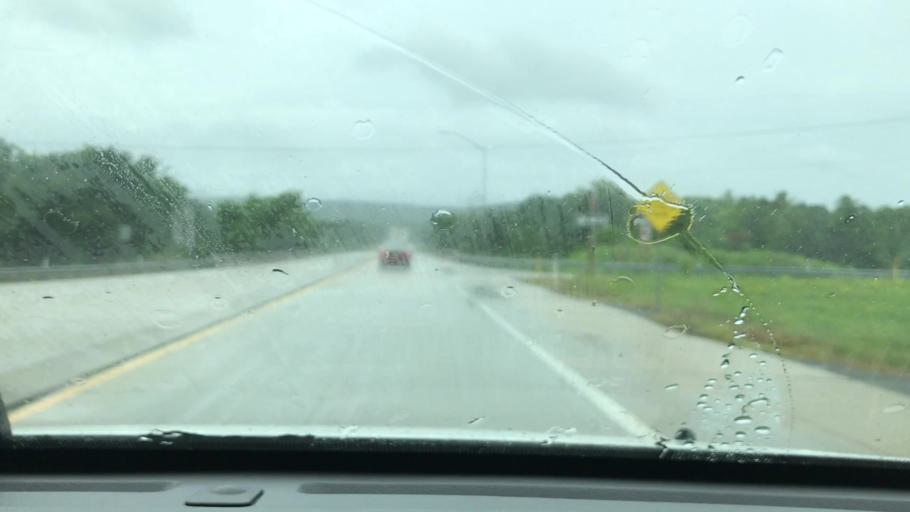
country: US
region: Pennsylvania
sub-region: Blair County
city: Tyrone
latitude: 40.7120
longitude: -78.1881
